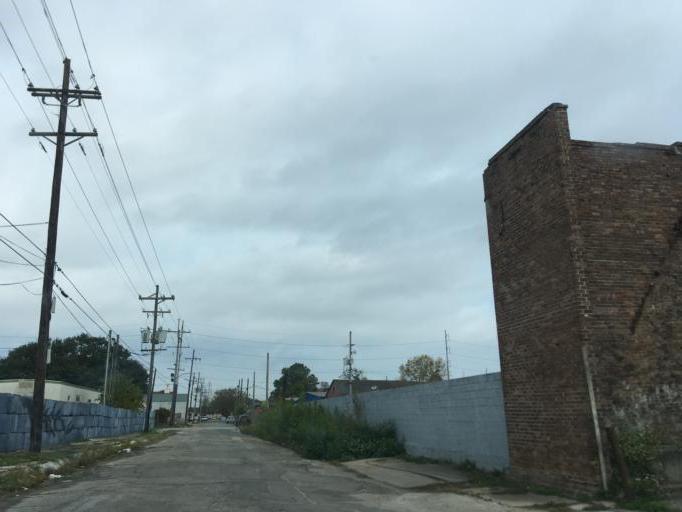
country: US
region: Louisiana
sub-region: Orleans Parish
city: New Orleans
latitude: 29.9870
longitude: -90.0596
